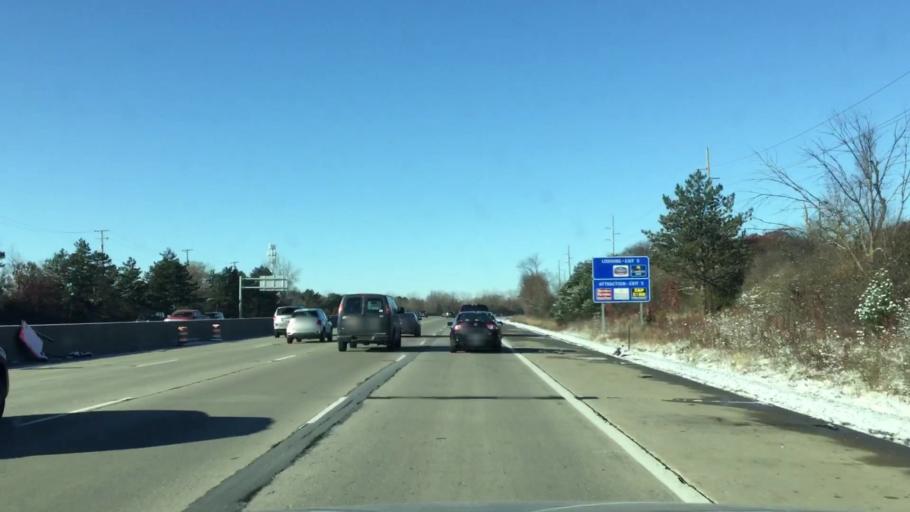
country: US
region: Michigan
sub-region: Oakland County
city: Franklin
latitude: 42.4909
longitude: -83.3258
